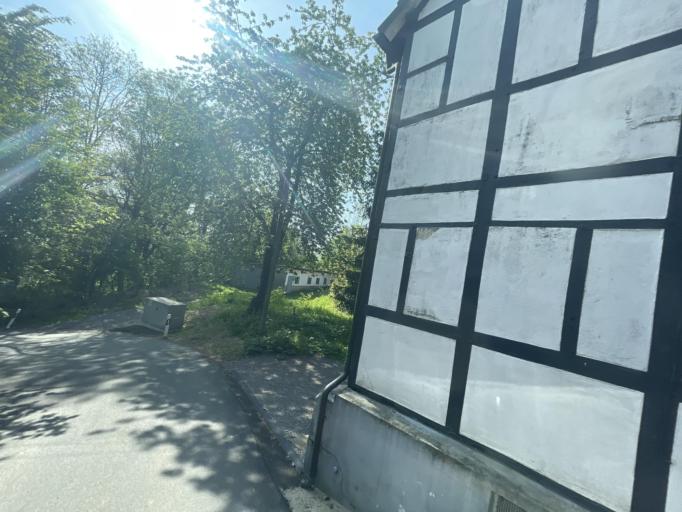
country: DE
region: North Rhine-Westphalia
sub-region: Regierungsbezirk Dusseldorf
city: Solingen
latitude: 51.1922
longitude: 7.0876
